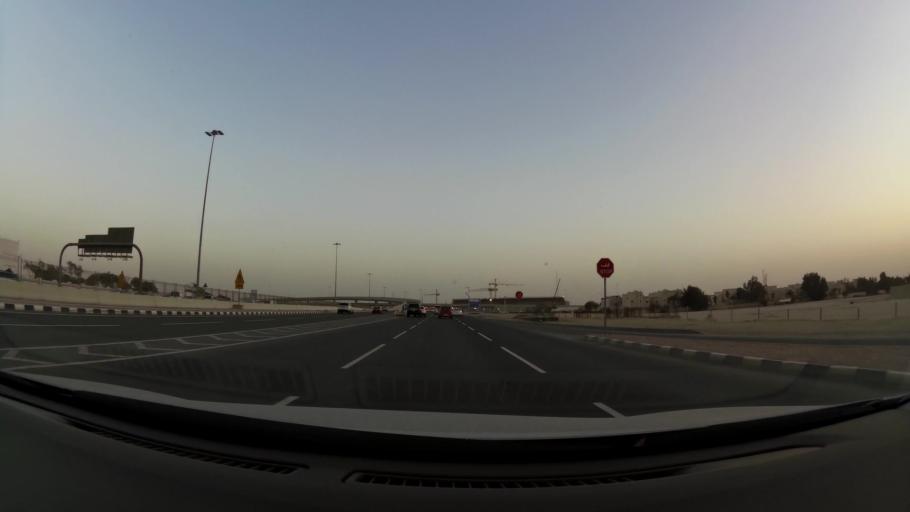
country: QA
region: Baladiyat ar Rayyan
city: Ar Rayyan
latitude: 25.3004
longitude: 51.4738
